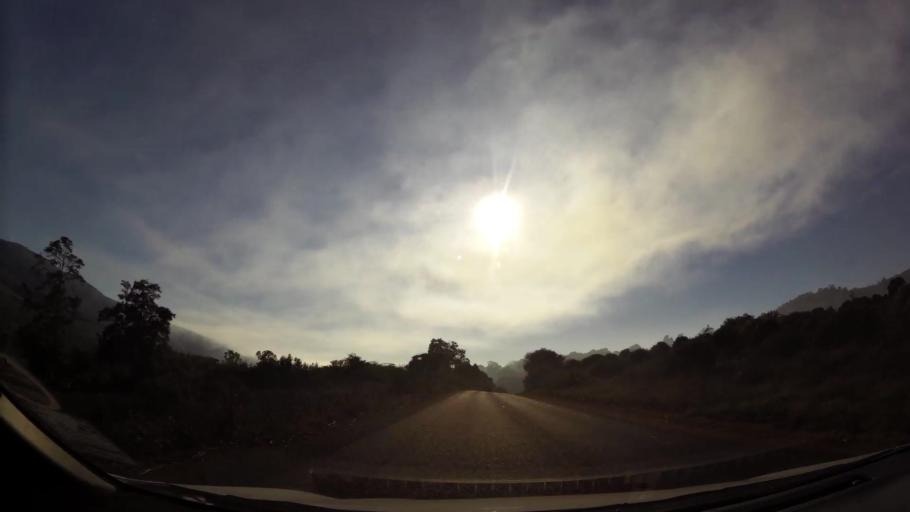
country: ZA
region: Limpopo
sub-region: Mopani District Municipality
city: Tzaneen
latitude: -23.9032
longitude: 30.0674
